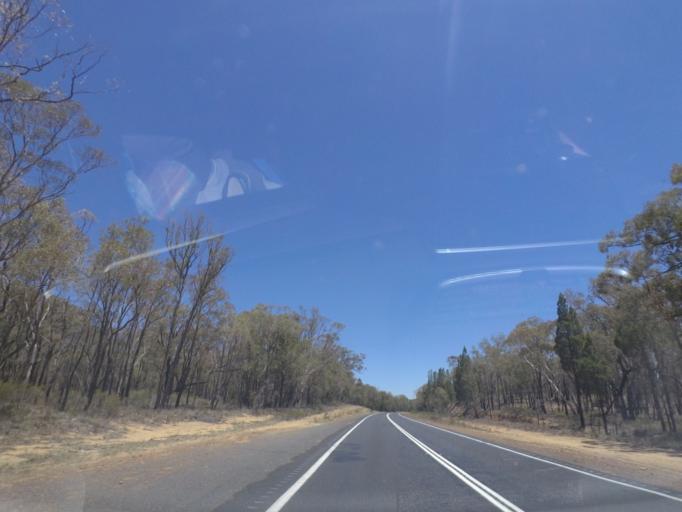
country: AU
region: New South Wales
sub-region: Warrumbungle Shire
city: Coonabarabran
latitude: -31.1927
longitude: 149.3529
